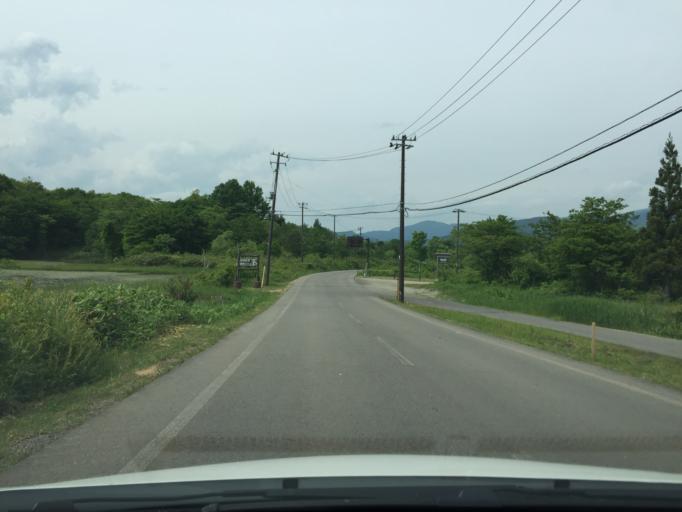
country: JP
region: Fukushima
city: Inawashiro
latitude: 37.6664
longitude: 140.0454
